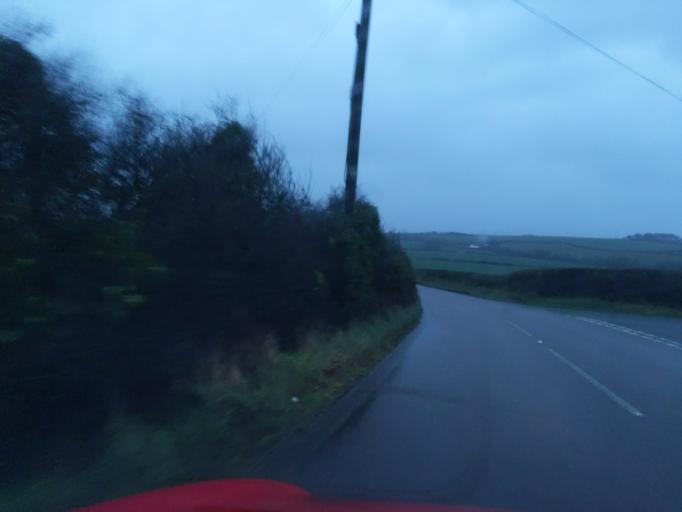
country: GB
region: England
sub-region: Cornwall
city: Saltash
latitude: 50.3619
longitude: -4.2667
